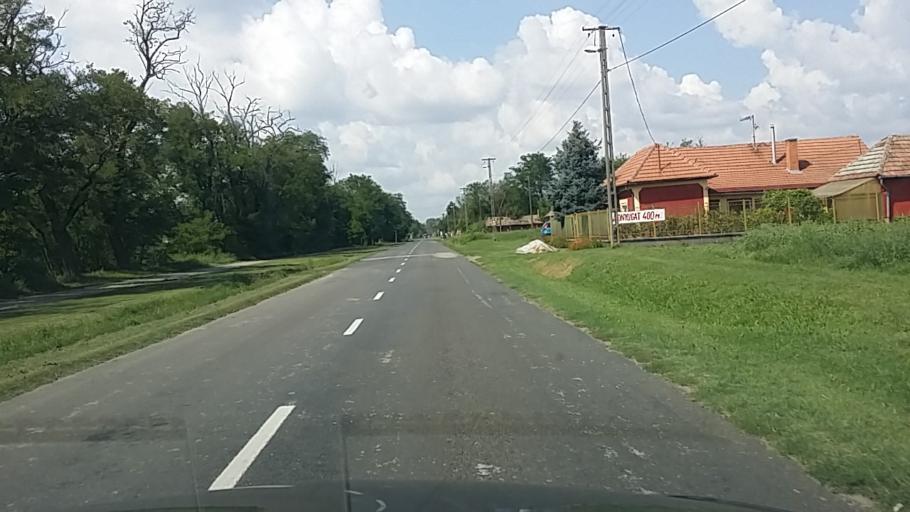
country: HU
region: Bacs-Kiskun
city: Tiszaalpar
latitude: 46.7487
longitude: 20.0414
